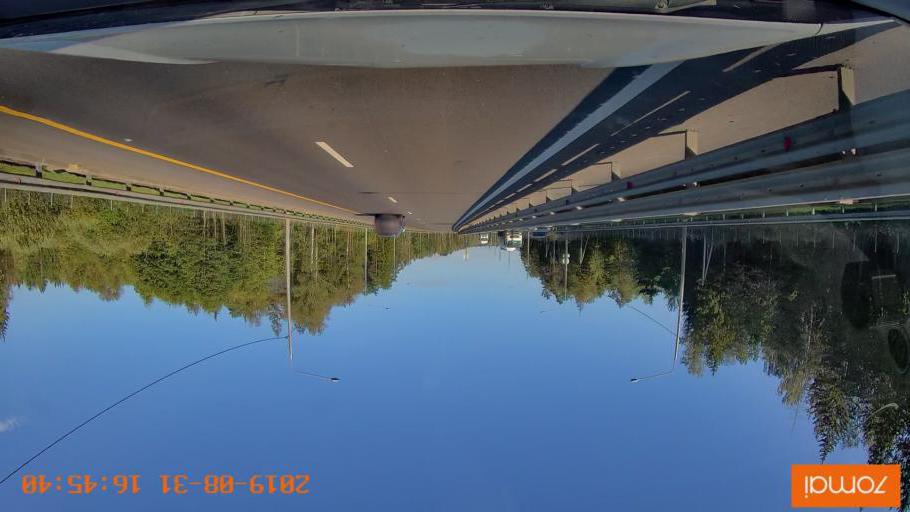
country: RU
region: Kaluga
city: Mstikhino
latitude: 54.6229
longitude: 36.1217
